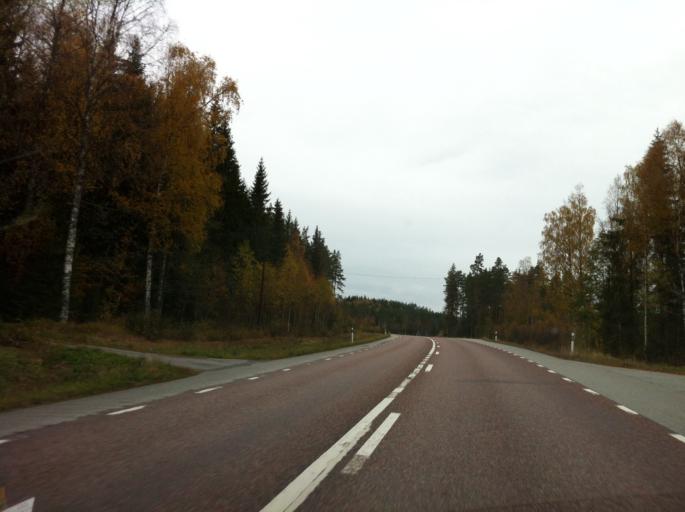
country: SE
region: Dalarna
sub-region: Ludvika Kommun
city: Grangesberg
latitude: 59.9973
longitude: 15.0118
